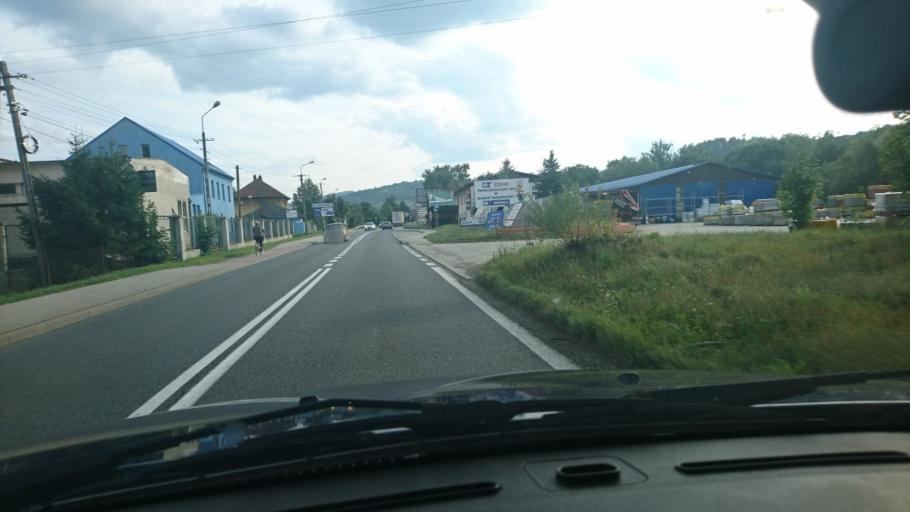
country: PL
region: Silesian Voivodeship
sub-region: Powiat zywiecki
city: Milowka
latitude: 49.5722
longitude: 19.0959
